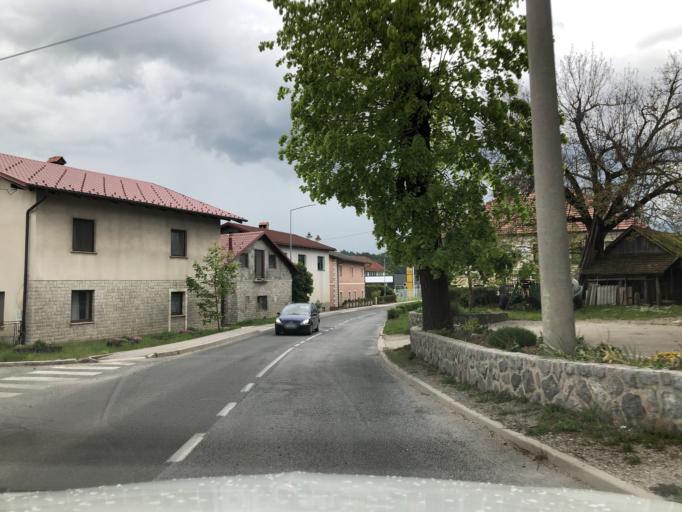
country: SI
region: Cerknica
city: Rakek
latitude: 45.8142
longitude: 14.3090
